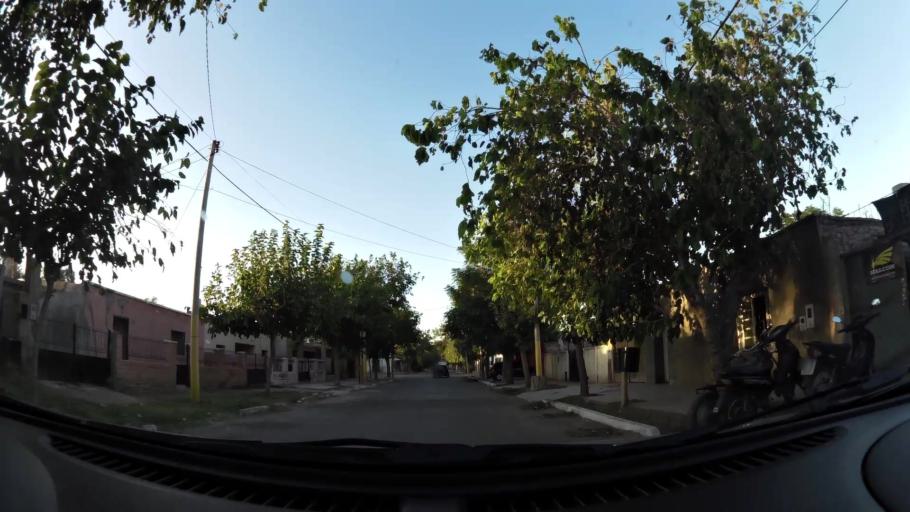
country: AR
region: San Juan
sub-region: Departamento de Santa Lucia
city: Santa Lucia
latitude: -31.5245
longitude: -68.5075
